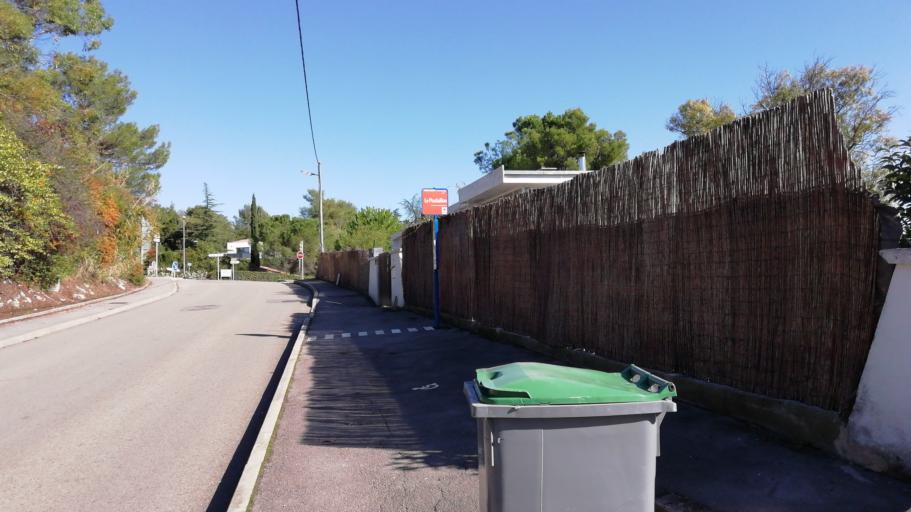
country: FR
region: Languedoc-Roussillon
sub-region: Departement de l'Herault
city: Prades-le-Lez
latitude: 43.7054
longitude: 3.8791
